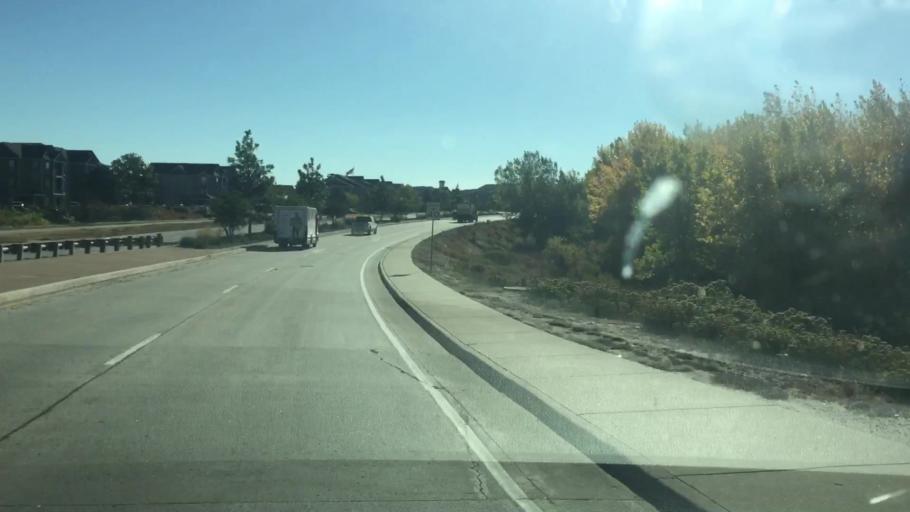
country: US
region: Colorado
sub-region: Douglas County
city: Parker
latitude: 39.5195
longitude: -104.7792
